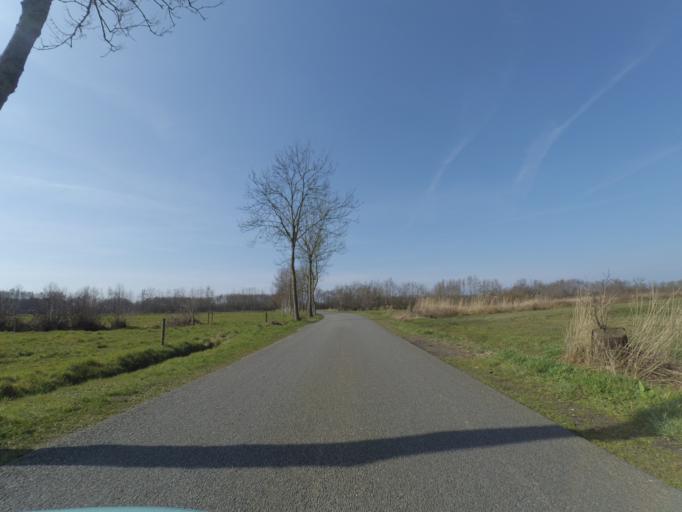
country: NL
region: Gelderland
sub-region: Gemeente Barneveld
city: Zwartebroek
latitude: 52.1861
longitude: 5.5057
